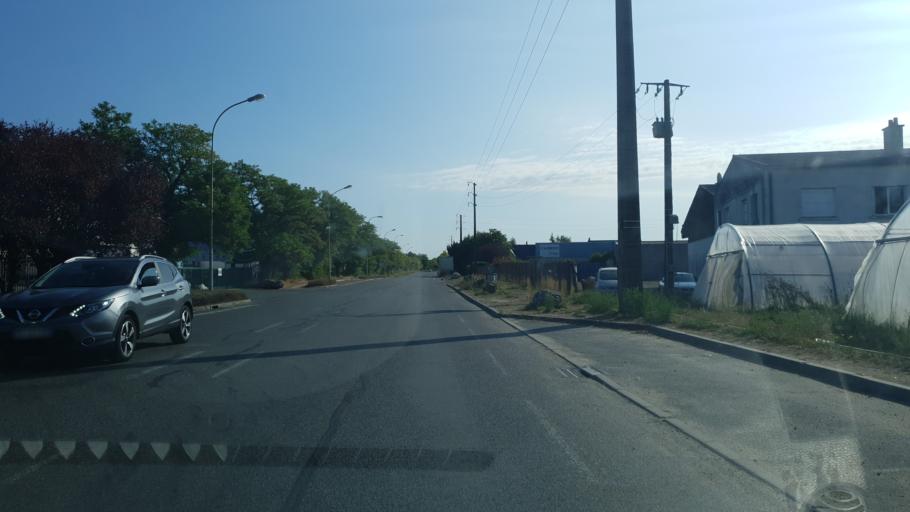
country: FR
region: Centre
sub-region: Departement d'Indre-et-Loire
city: Saint-Pierre-des-Corps
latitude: 47.3868
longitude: 0.7588
